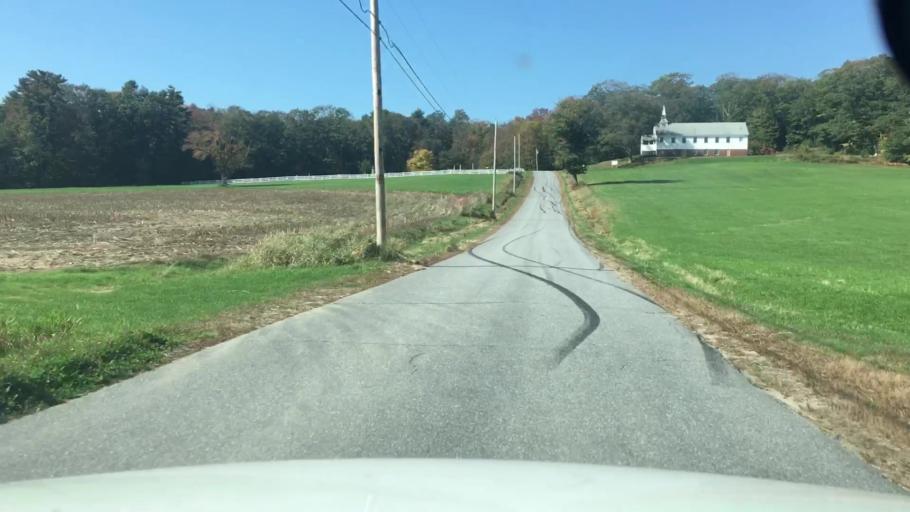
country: US
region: Maine
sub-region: Sagadahoc County
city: Topsham
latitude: 44.0138
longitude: -69.9713
